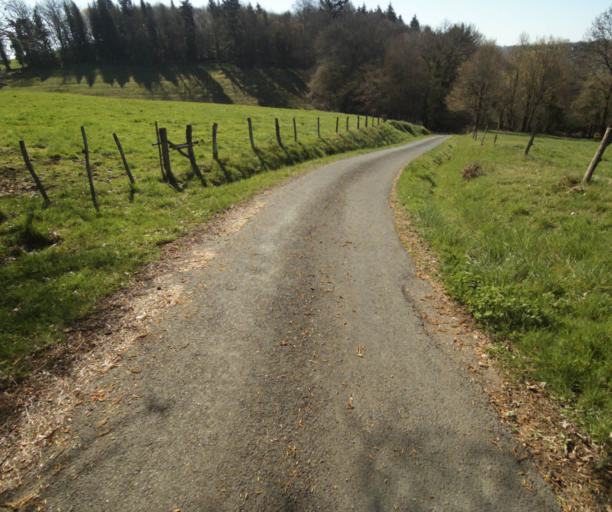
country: FR
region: Limousin
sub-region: Departement de la Correze
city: Seilhac
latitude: 45.3850
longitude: 1.7510
